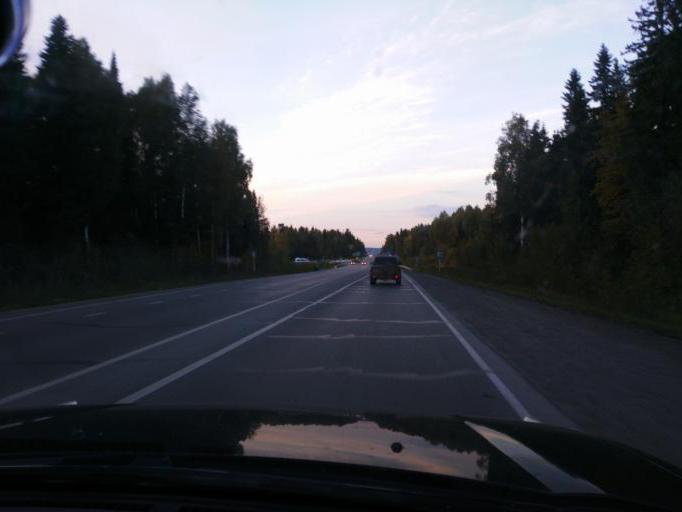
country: RU
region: Perm
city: Polazna
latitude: 58.1356
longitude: 56.4212
